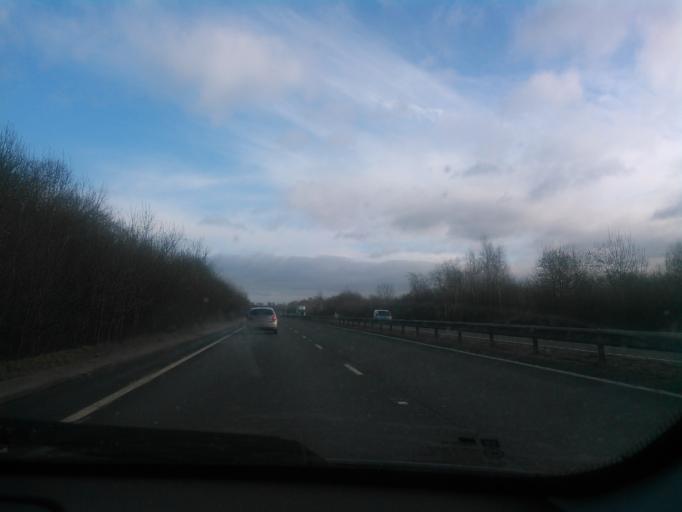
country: GB
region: England
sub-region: Derbyshire
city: Rodsley
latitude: 52.8821
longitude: -1.6951
